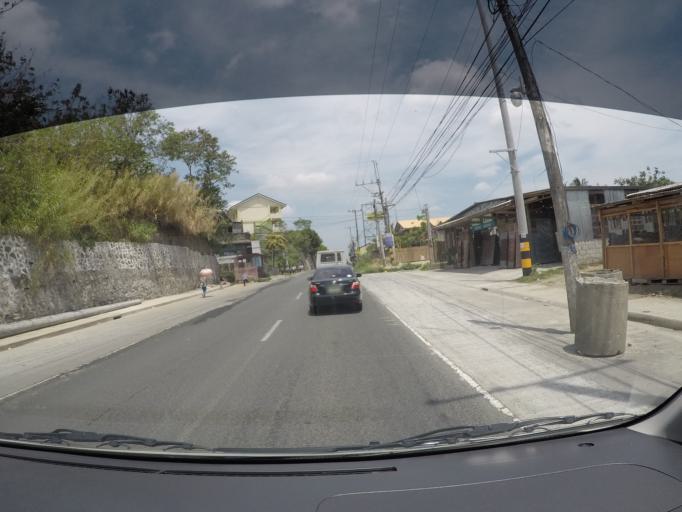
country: PH
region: Calabarzon
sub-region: Province of Cavite
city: Puting Kahoy
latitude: 14.2024
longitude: 121.0231
